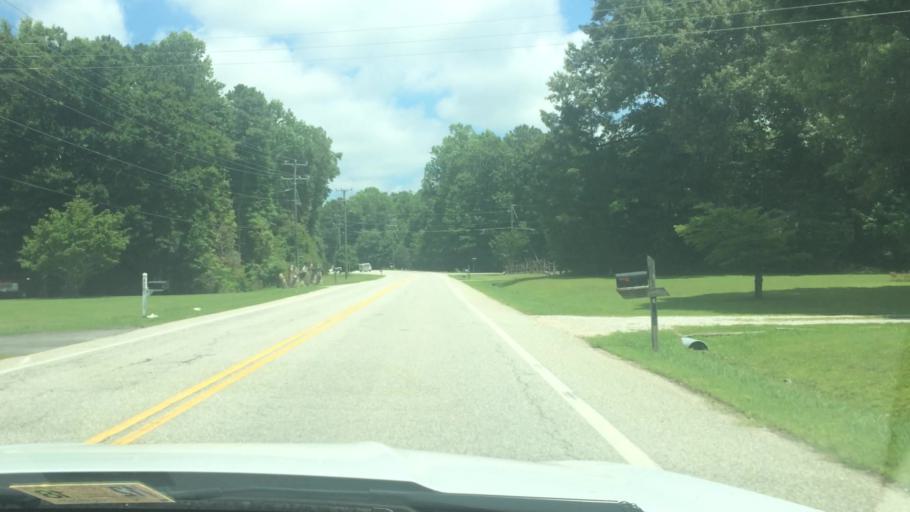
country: US
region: Virginia
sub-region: James City County
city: Williamsburg
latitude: 37.2880
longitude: -76.8007
